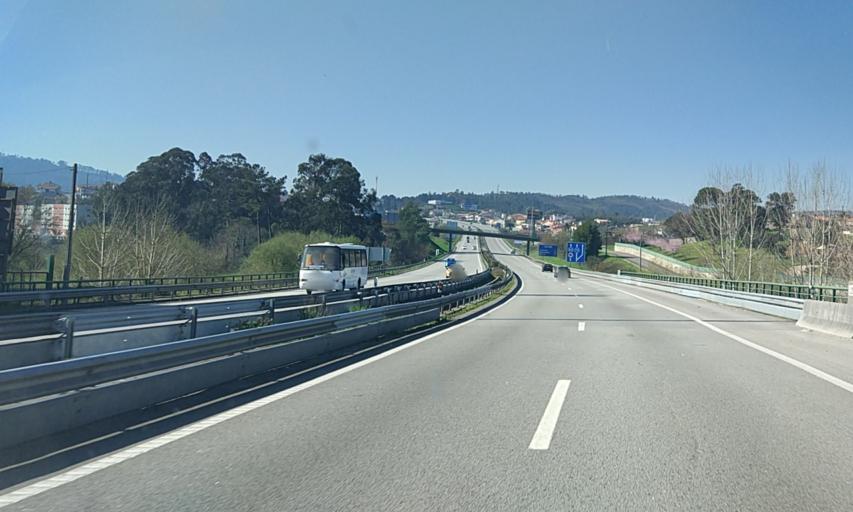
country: PT
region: Porto
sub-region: Valongo
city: Campo
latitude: 41.1848
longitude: -8.4566
